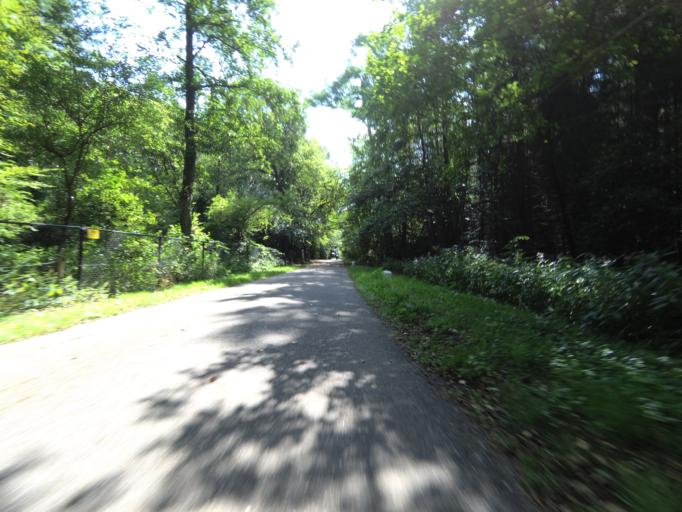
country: NL
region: Overijssel
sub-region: Gemeente Hengelo
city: Hengelo
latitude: 52.2478
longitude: 6.8369
